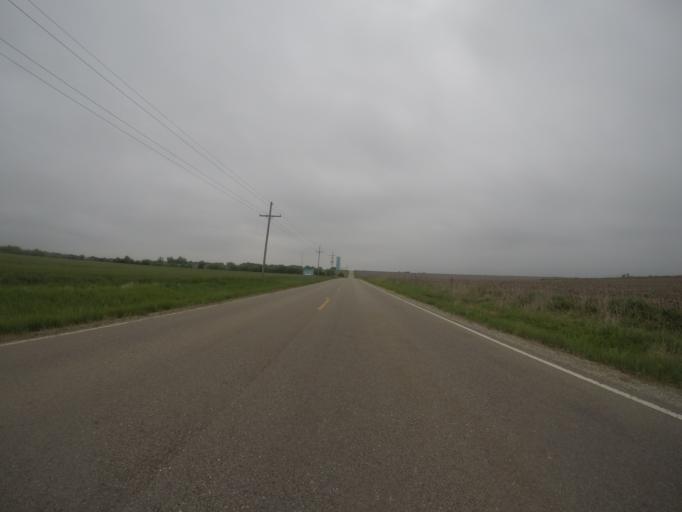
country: US
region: Kansas
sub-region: Pottawatomie County
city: Westmoreland
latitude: 39.5222
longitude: -96.2835
